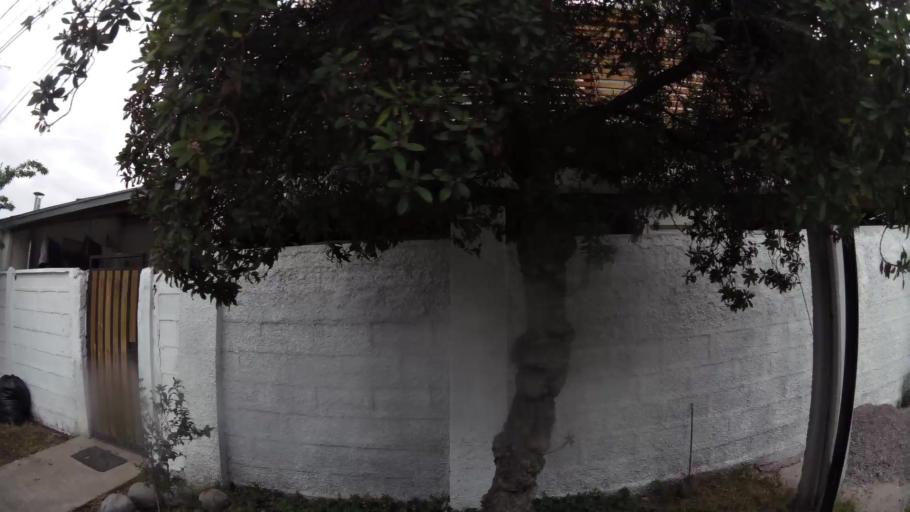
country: CL
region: Santiago Metropolitan
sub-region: Provincia de Santiago
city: Villa Presidente Frei, Nunoa, Santiago, Chile
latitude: -33.5131
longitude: -70.5972
